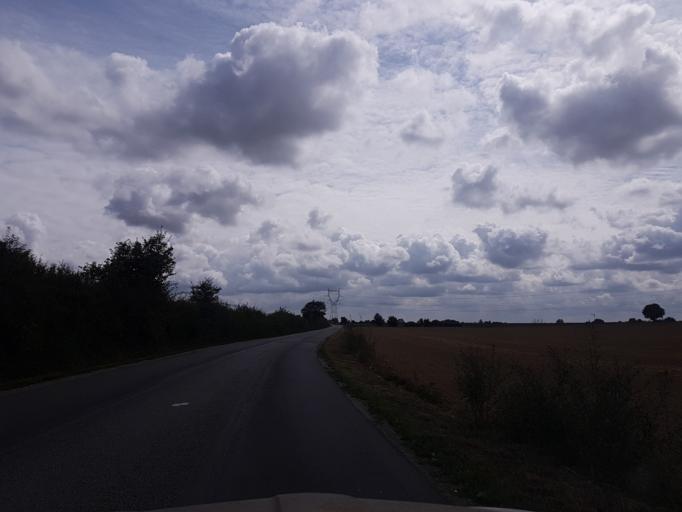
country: FR
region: Pays de la Loire
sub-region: Departement de la Loire-Atlantique
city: Les Touches
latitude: 47.4268
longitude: -1.4424
